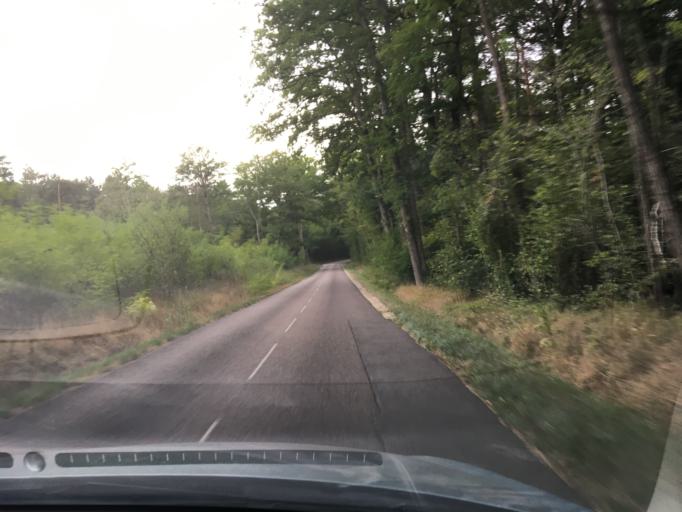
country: FR
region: Bourgogne
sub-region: Departement de l'Yonne
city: Appoigny
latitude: 47.8722
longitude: 3.4990
